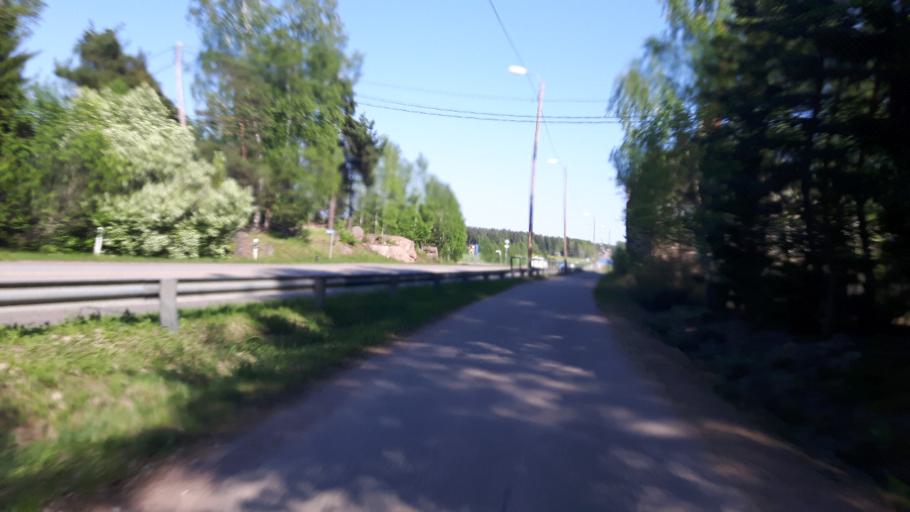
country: FI
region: Kymenlaakso
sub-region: Kotka-Hamina
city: Broby
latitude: 60.4969
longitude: 26.7893
